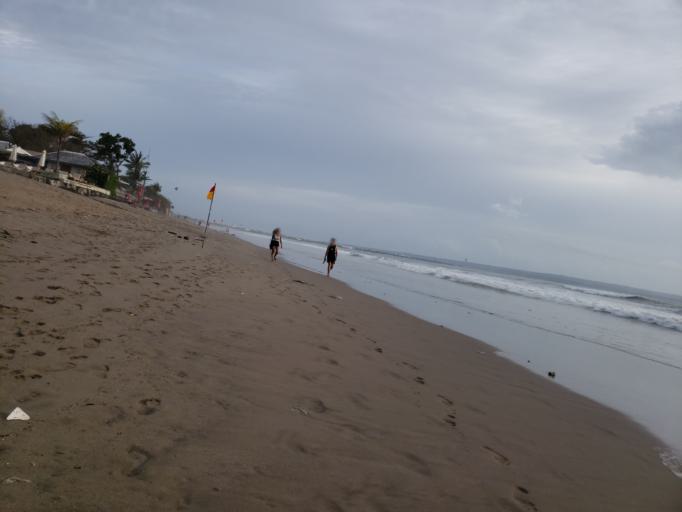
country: ID
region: Bali
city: Kuta
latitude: -8.6863
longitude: 115.1535
